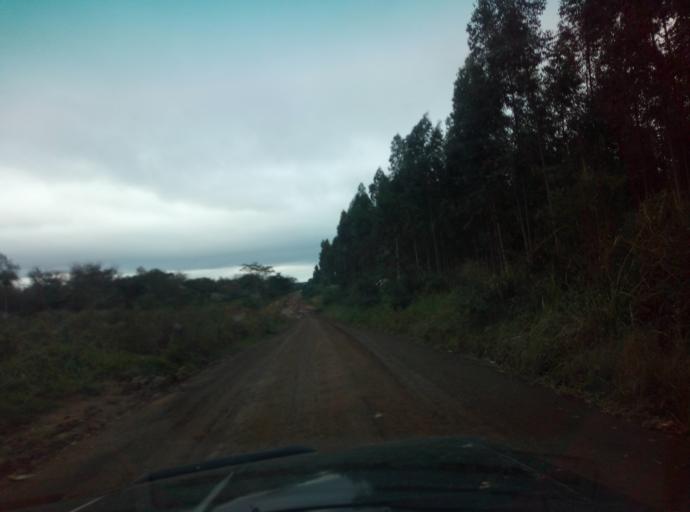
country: PY
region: Caaguazu
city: Carayao
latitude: -25.1902
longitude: -56.3861
